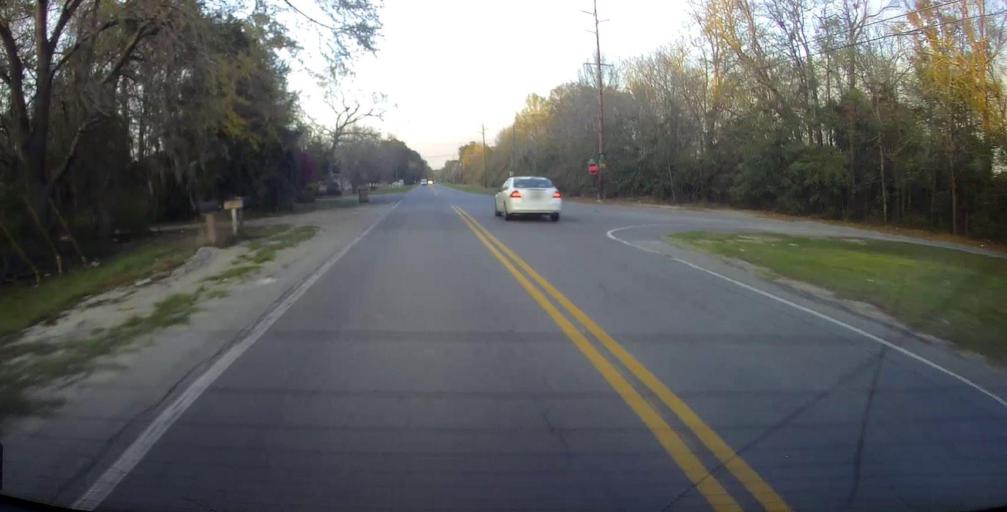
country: US
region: Georgia
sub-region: Chatham County
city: Bloomingdale
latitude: 32.1519
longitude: -81.3885
